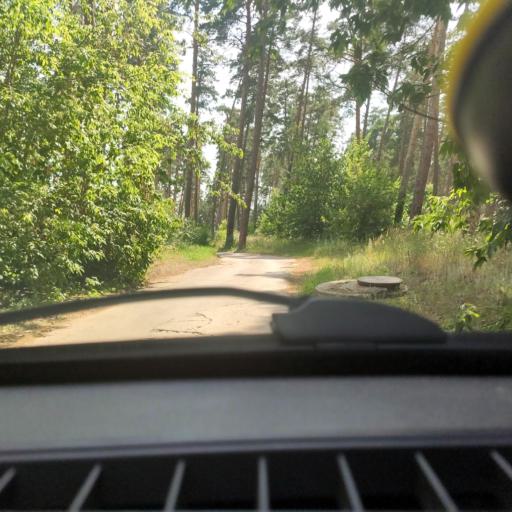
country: RU
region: Samara
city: Tol'yatti
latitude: 53.4747
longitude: 49.3433
